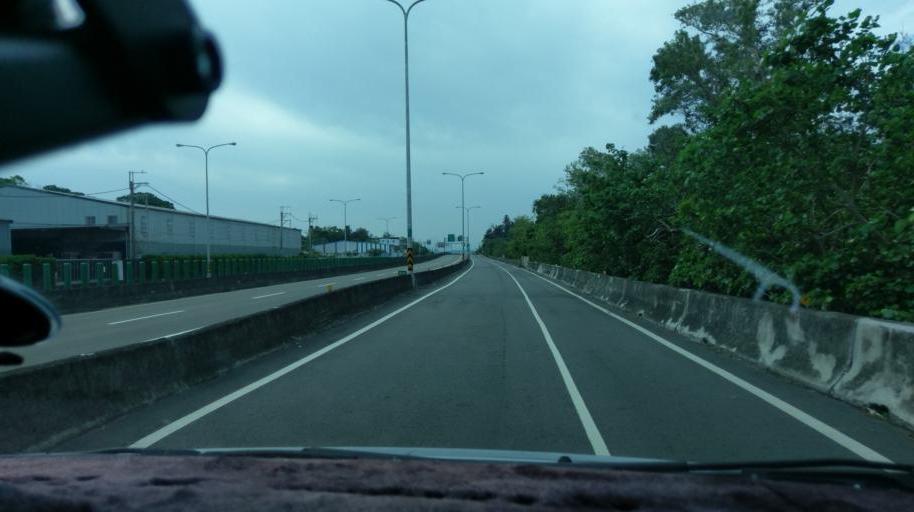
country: TW
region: Taiwan
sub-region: Hsinchu
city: Hsinchu
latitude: 24.7207
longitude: 120.8682
